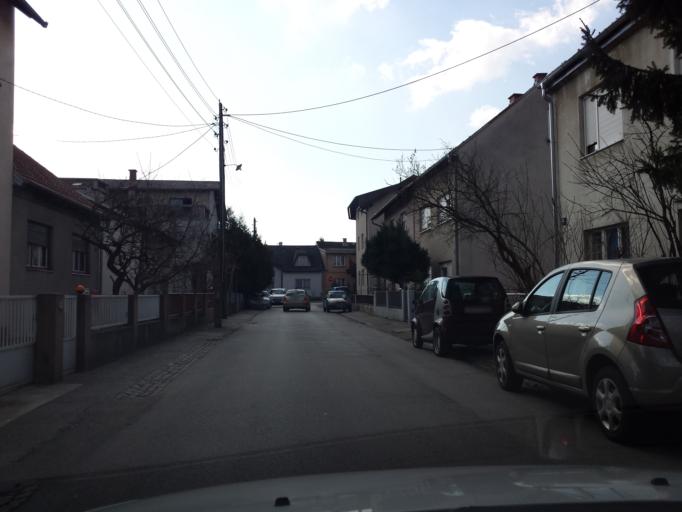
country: HR
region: Grad Zagreb
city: Jankomir
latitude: 45.7993
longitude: 15.9331
